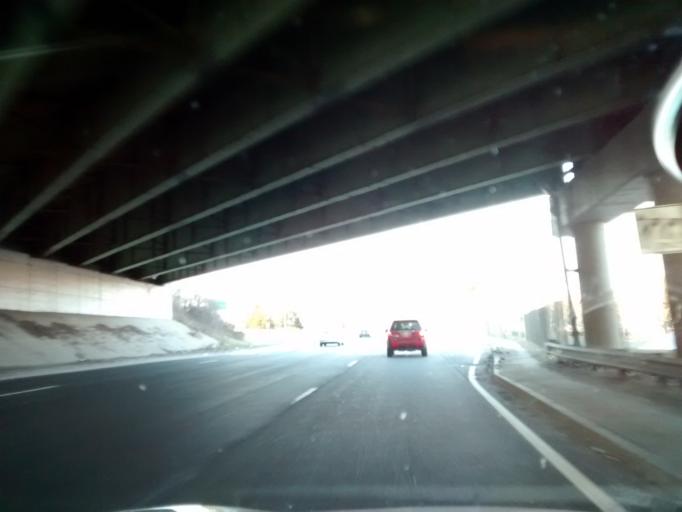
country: US
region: Massachusetts
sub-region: Worcester County
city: Worcester
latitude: 42.2965
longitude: -71.8031
